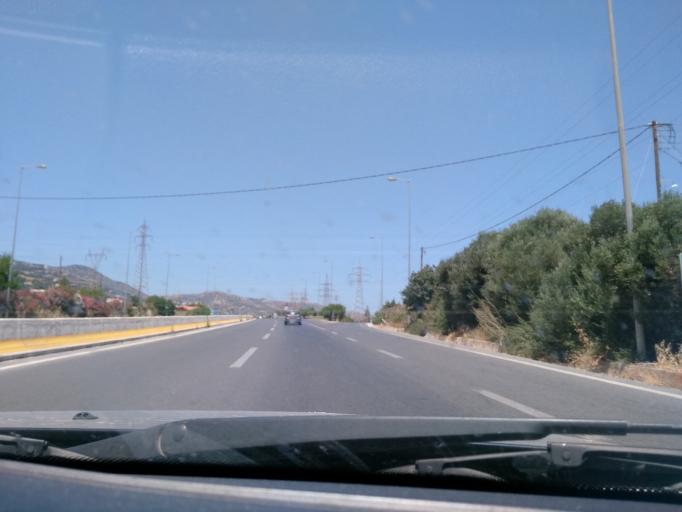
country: GR
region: Crete
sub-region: Nomos Irakleiou
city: Gazi
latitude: 35.3363
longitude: 25.0513
